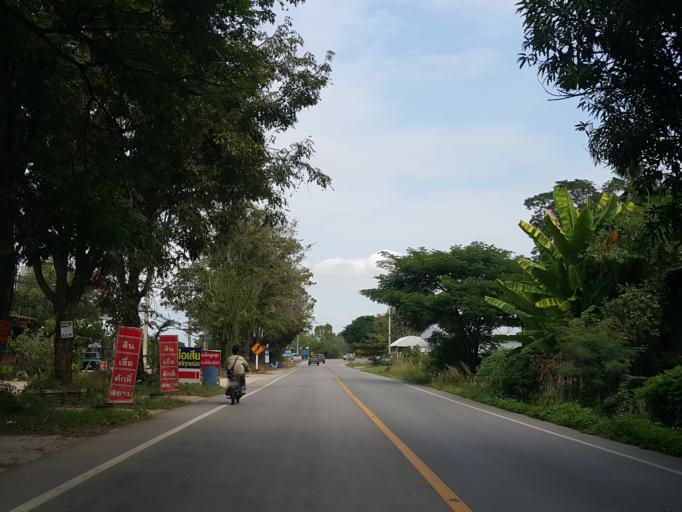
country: TH
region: Lampang
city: Lampang
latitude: 18.3158
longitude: 99.4633
